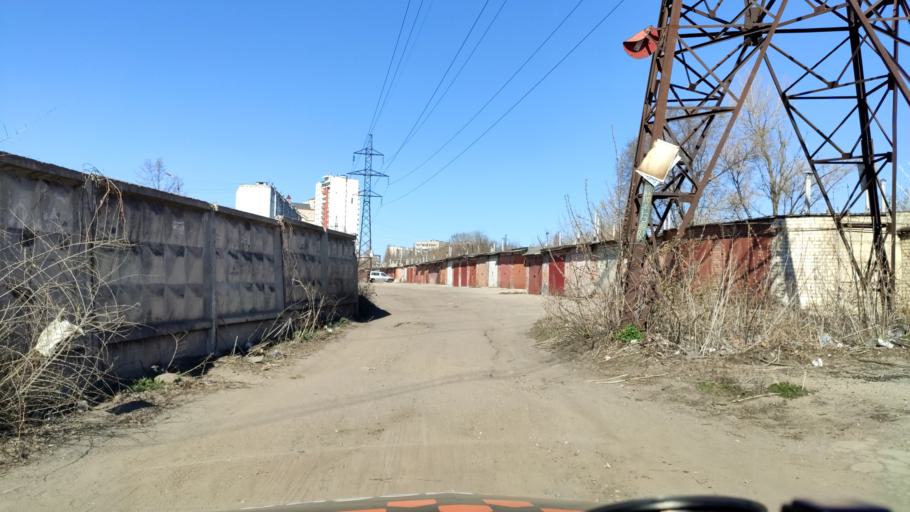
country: RU
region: Voronezj
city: Voronezh
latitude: 51.6441
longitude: 39.1572
